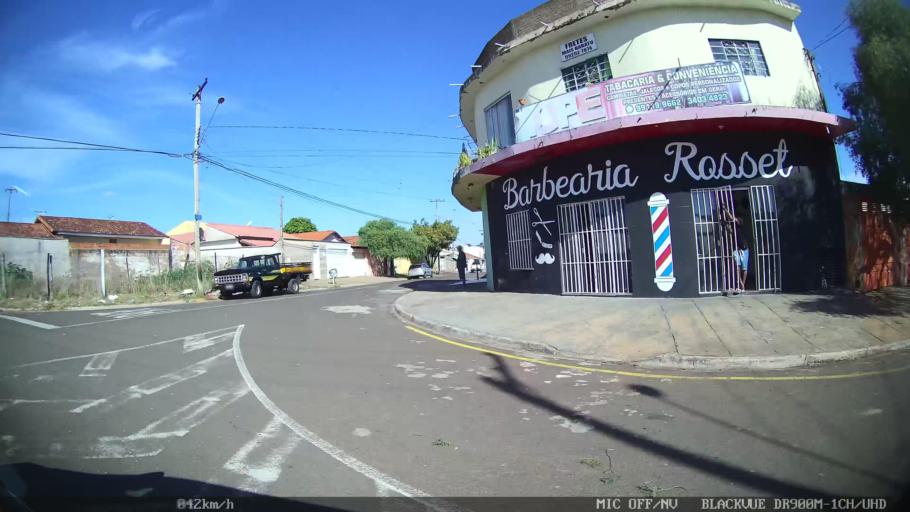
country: BR
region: Sao Paulo
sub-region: Franca
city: Franca
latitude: -20.4890
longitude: -47.4233
